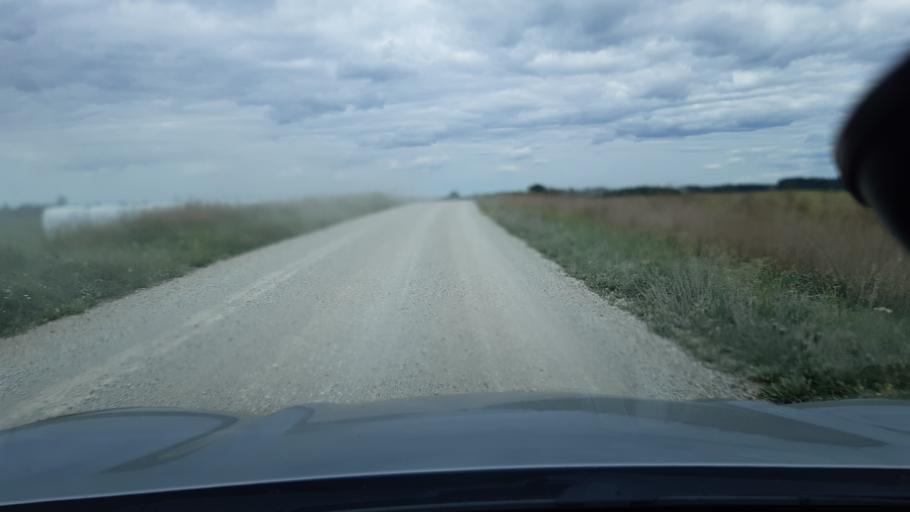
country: EE
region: Raplamaa
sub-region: Maerjamaa vald
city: Marjamaa
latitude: 58.9302
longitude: 24.3068
